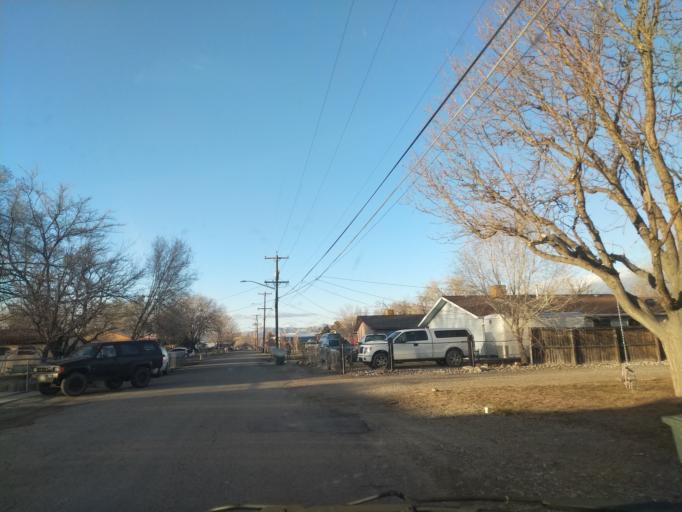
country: US
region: Colorado
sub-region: Mesa County
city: Fruitvale
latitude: 39.0749
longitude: -108.5210
